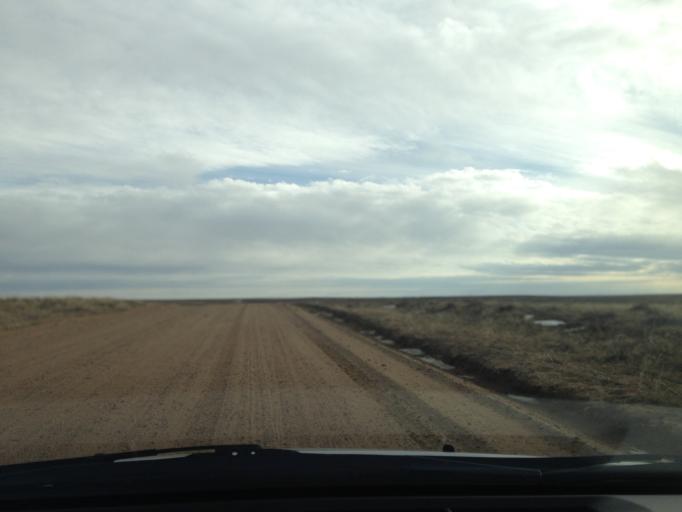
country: US
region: Colorado
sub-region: Weld County
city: Keenesburg
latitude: 40.2379
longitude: -104.2068
